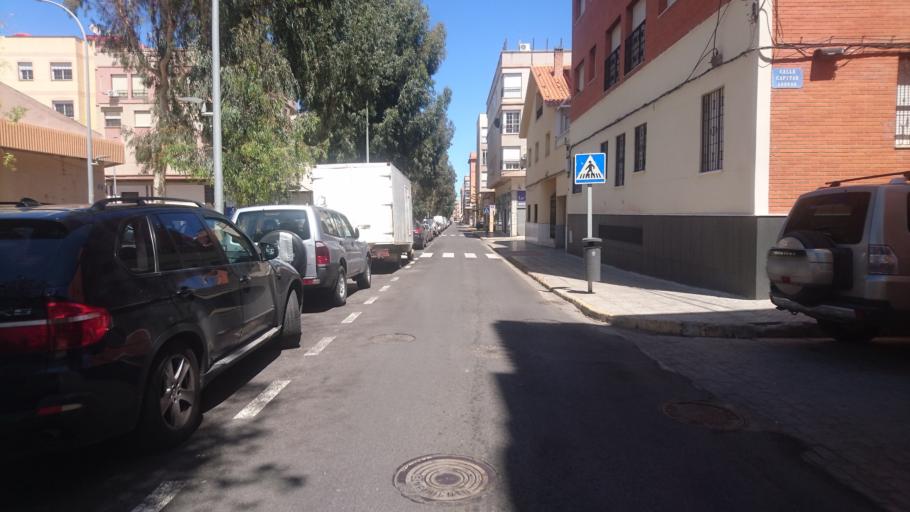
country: ES
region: Melilla
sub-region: Melilla
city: Melilla
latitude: 35.2743
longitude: -2.9426
